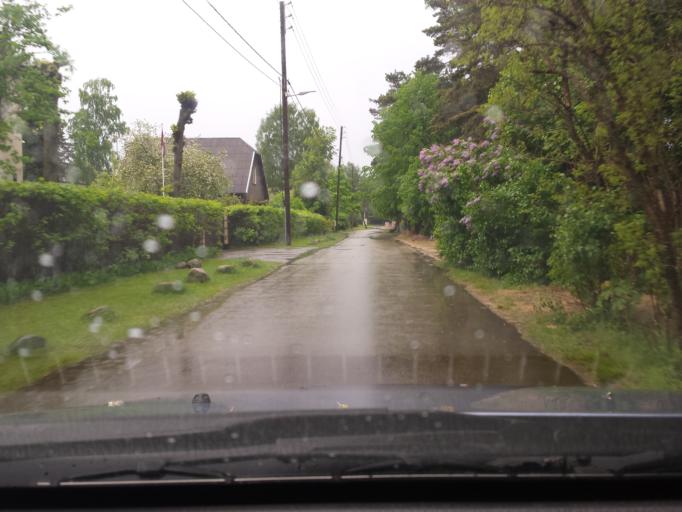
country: LV
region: Riga
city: Bolderaja
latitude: 57.0745
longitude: 24.0979
